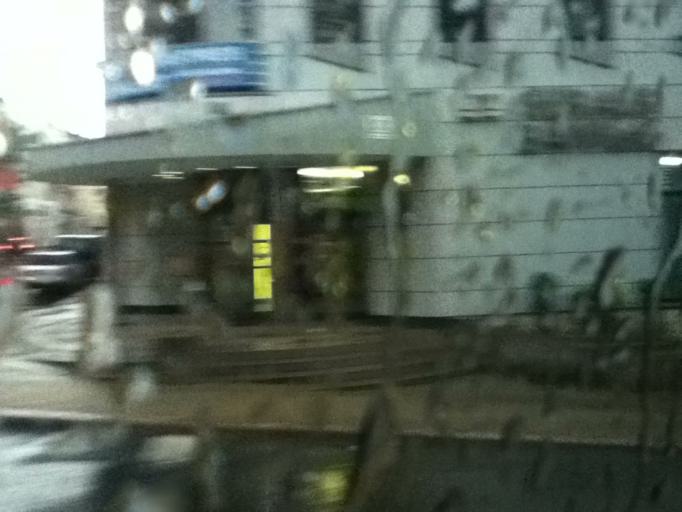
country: DE
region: Thuringia
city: Gera
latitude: 50.8810
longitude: 12.0837
